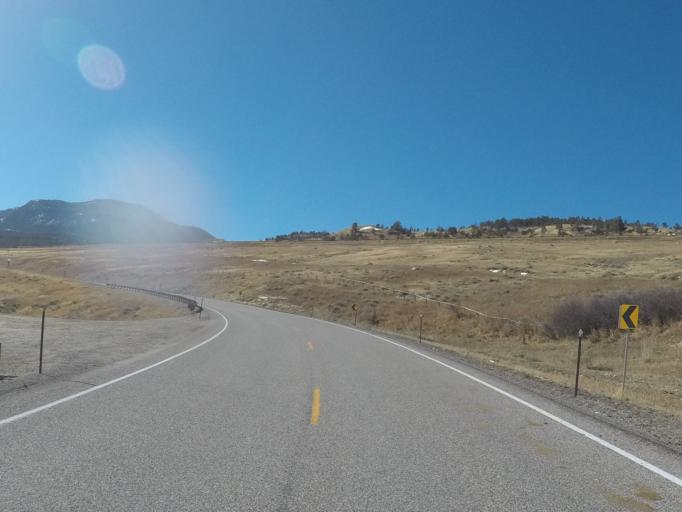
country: US
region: Wyoming
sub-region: Park County
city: Cody
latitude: 44.7237
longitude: -109.3059
